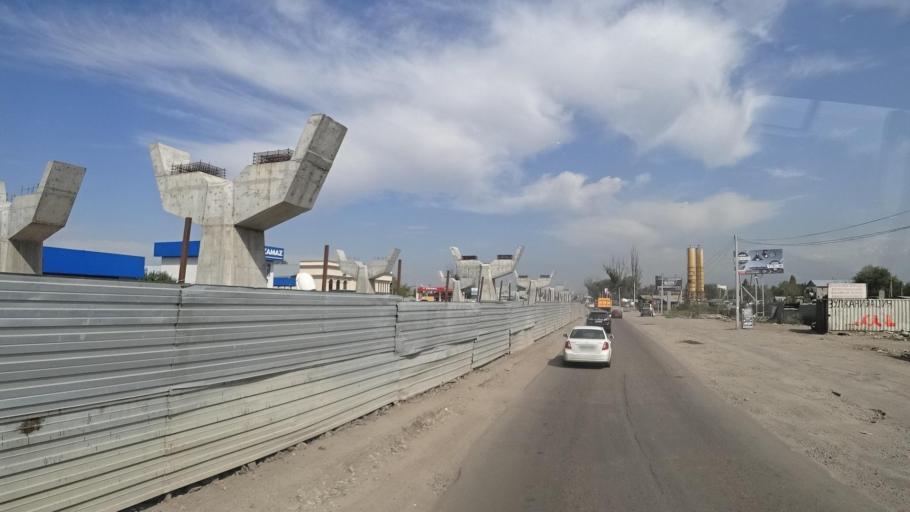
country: KZ
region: Almaty Oblysy
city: Burunday
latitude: 43.2288
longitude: 76.7628
